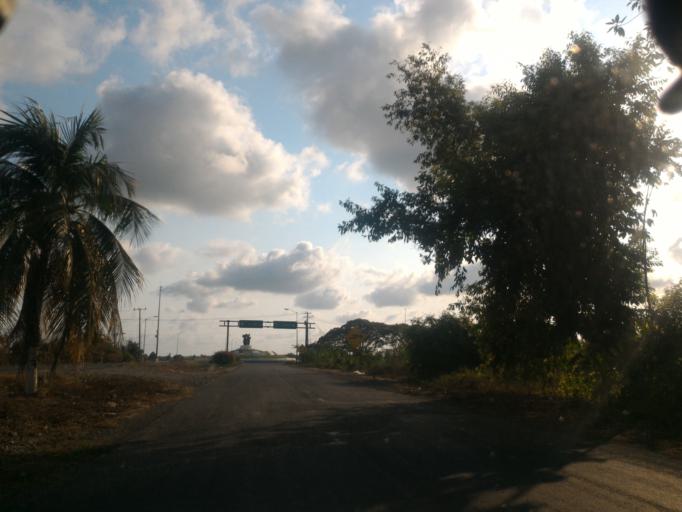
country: MX
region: Colima
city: Tecoman
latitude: 18.8989
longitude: -103.8588
